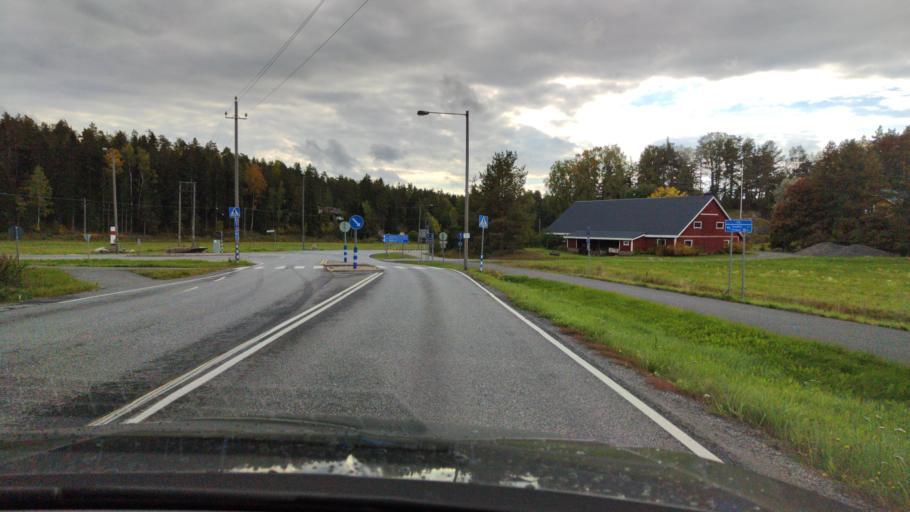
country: FI
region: Varsinais-Suomi
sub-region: Turku
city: Raisio
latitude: 60.3591
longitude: 22.1757
